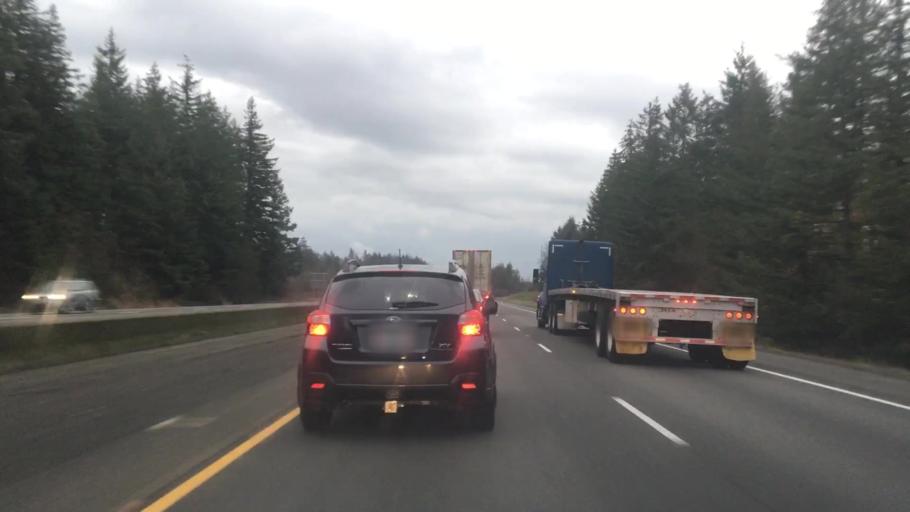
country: US
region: Washington
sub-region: Lewis County
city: Napavine
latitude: 46.5348
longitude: -122.8768
